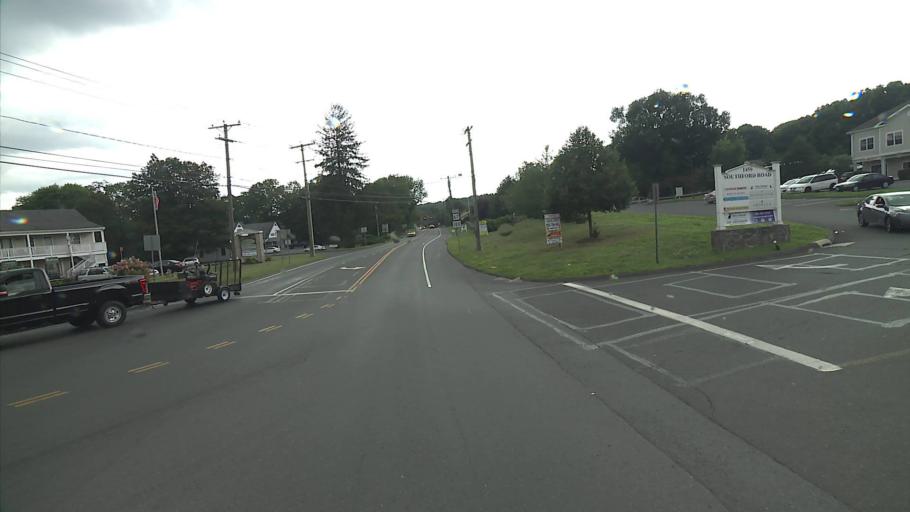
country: US
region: Connecticut
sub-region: New Haven County
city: Southbury
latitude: 41.4648
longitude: -73.1624
